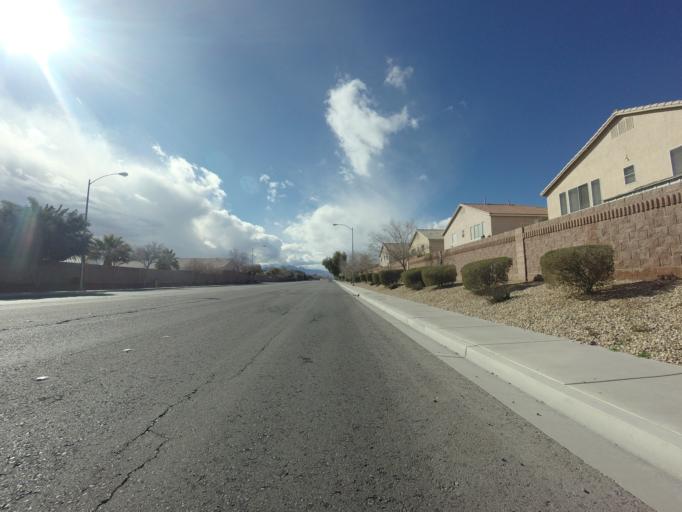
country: US
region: Nevada
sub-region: Clark County
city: North Las Vegas
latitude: 36.2543
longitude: -115.1279
